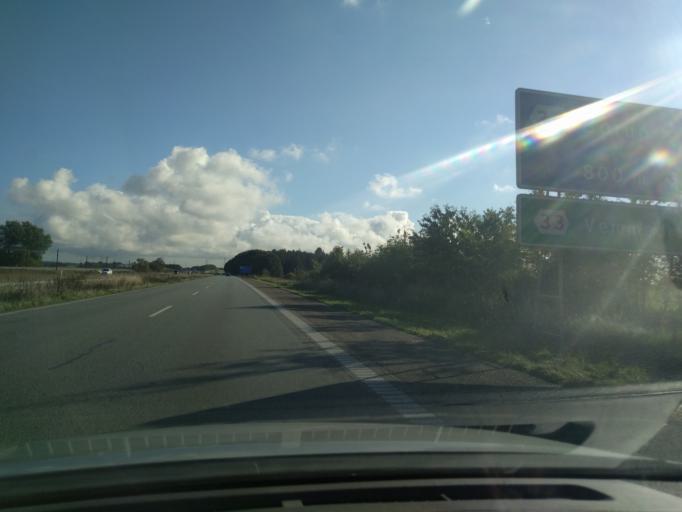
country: DK
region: Zealand
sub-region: Koge Kommune
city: Borup
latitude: 55.4567
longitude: 11.9495
